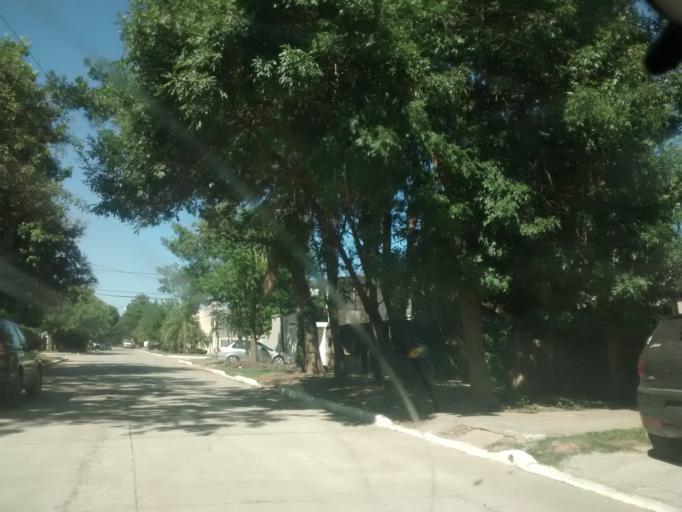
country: AR
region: Chaco
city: Resistencia
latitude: -27.4388
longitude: -58.9710
